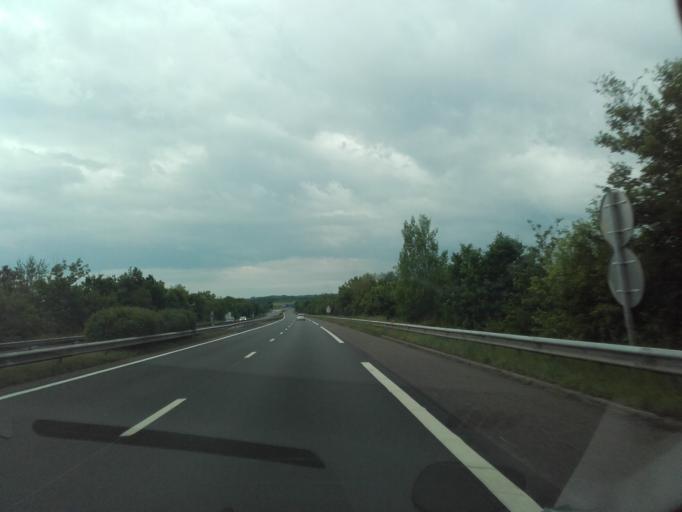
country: FR
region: Rhone-Alpes
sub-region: Departement de la Loire
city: Saint-Germain-Laval
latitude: 45.8306
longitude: 4.1014
